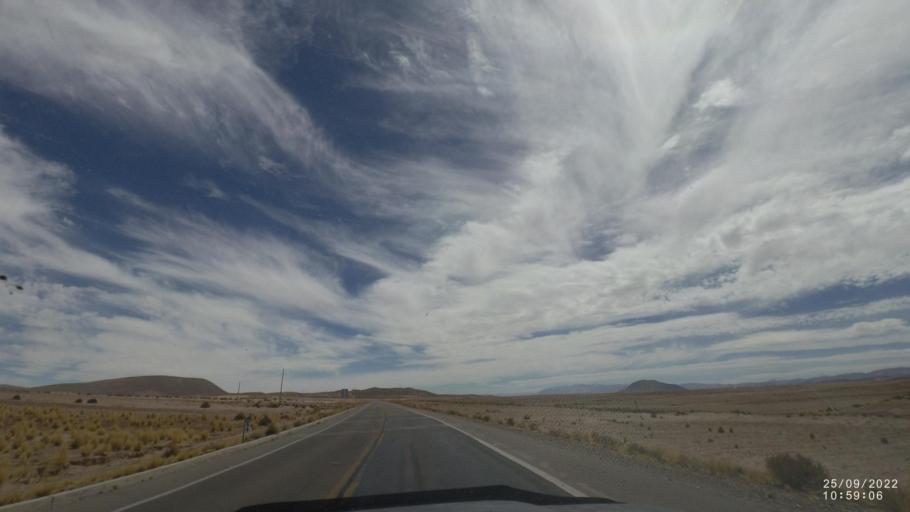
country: BO
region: Oruro
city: Challapata
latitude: -19.4544
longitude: -66.9092
